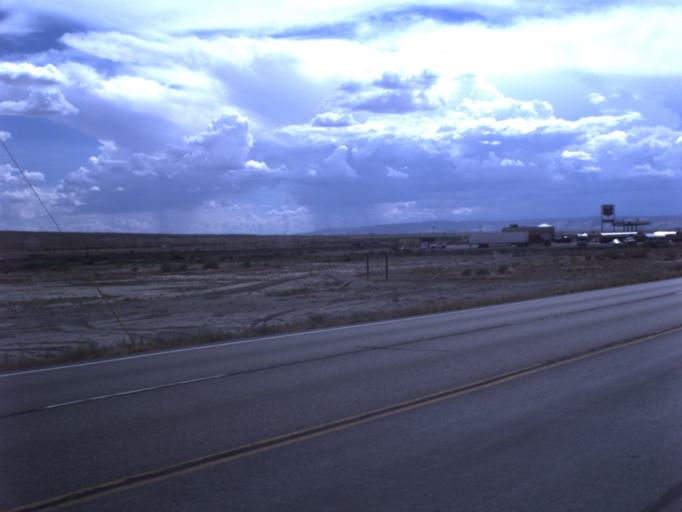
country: US
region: Utah
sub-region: Carbon County
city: East Carbon City
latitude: 38.9955
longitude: -110.1807
